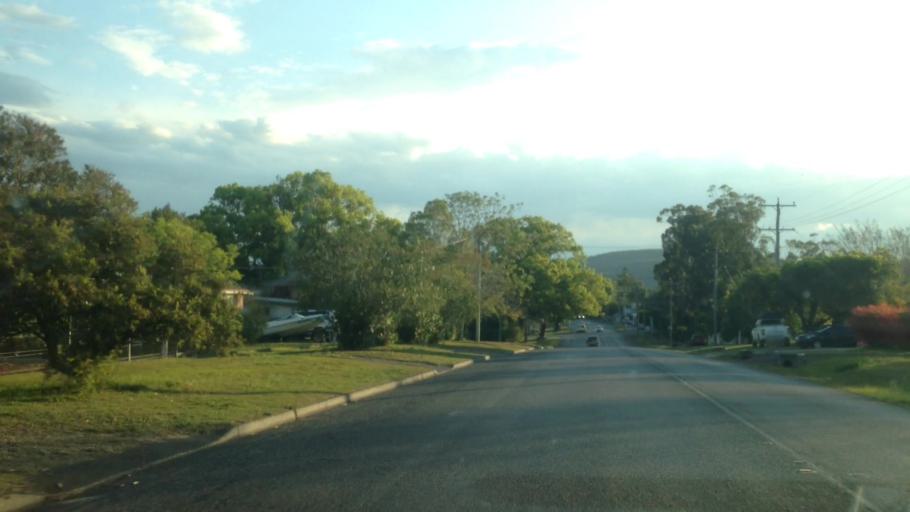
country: AU
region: New South Wales
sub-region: Lake Macquarie Shire
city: Cooranbong
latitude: -33.0683
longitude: 151.4659
